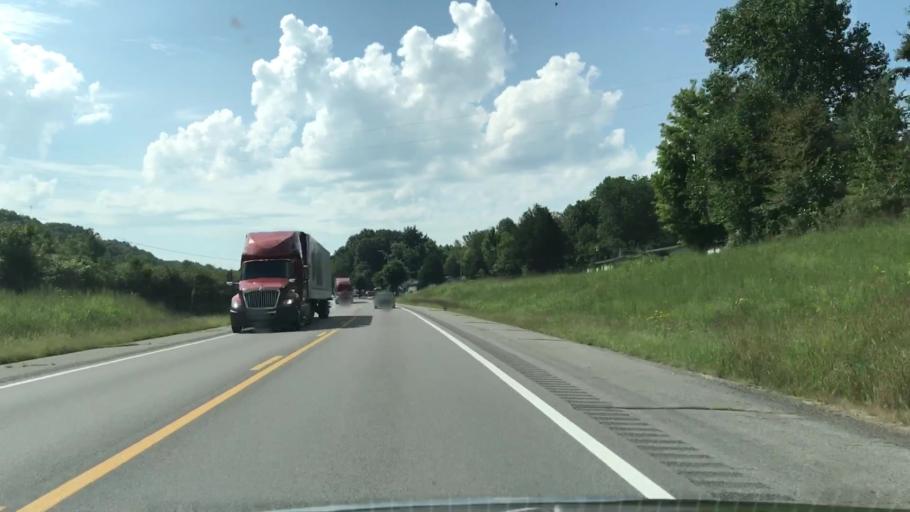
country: US
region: Tennessee
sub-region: Sumner County
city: Westmoreland
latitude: 36.6371
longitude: -86.2431
